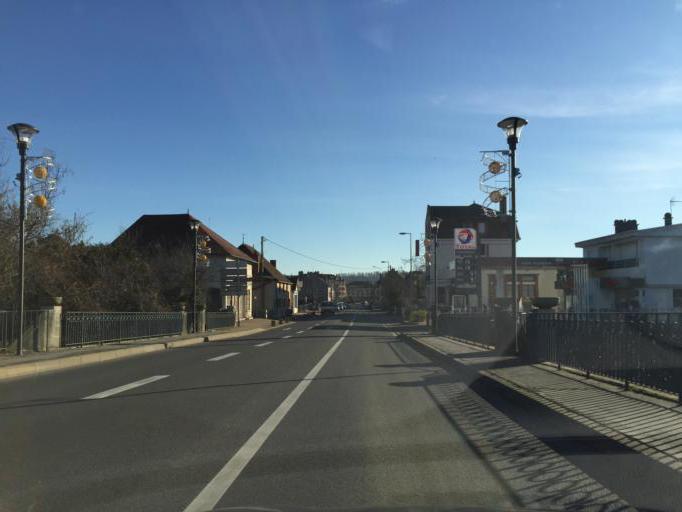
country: FR
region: Auvergne
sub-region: Departement de l'Allier
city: Saint-Pourcain-sur-Sioule
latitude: 46.3068
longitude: 3.2938
